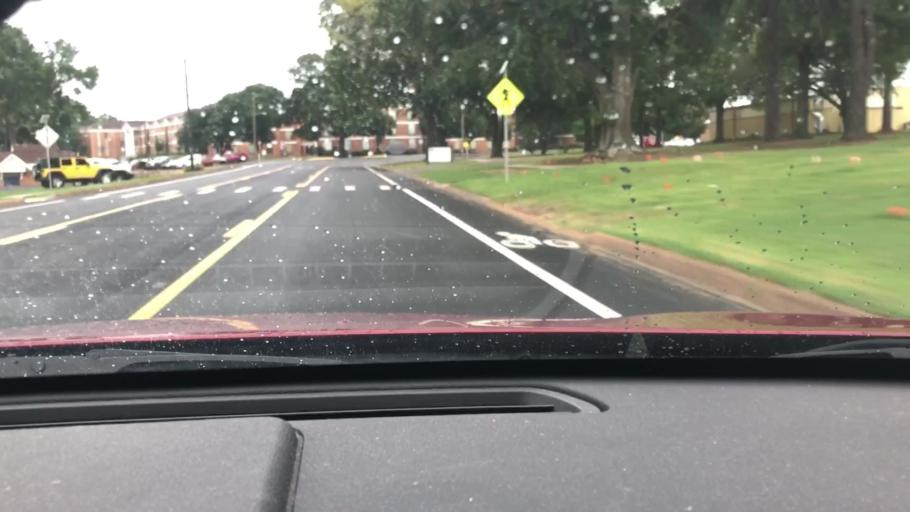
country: US
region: Arkansas
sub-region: Columbia County
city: Magnolia
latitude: 33.2942
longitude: -93.2373
